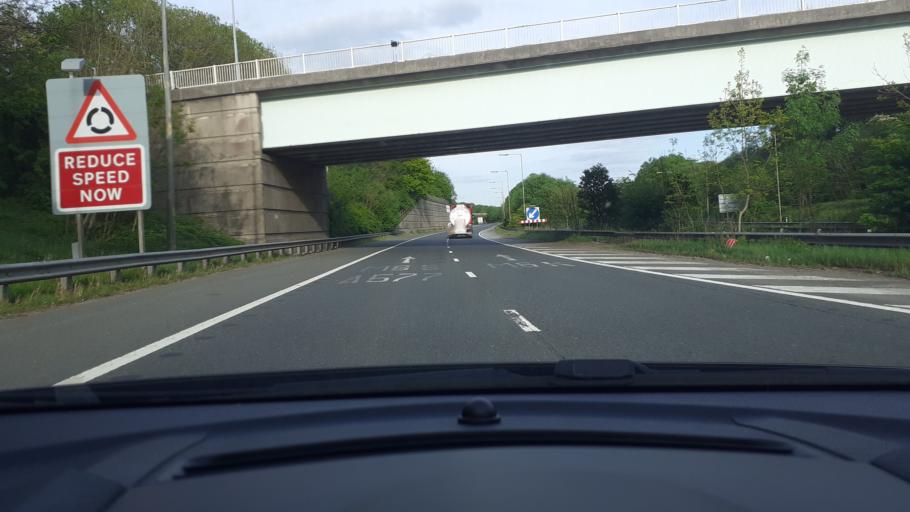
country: GB
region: England
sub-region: St. Helens
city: Billinge
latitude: 53.5364
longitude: -2.7079
